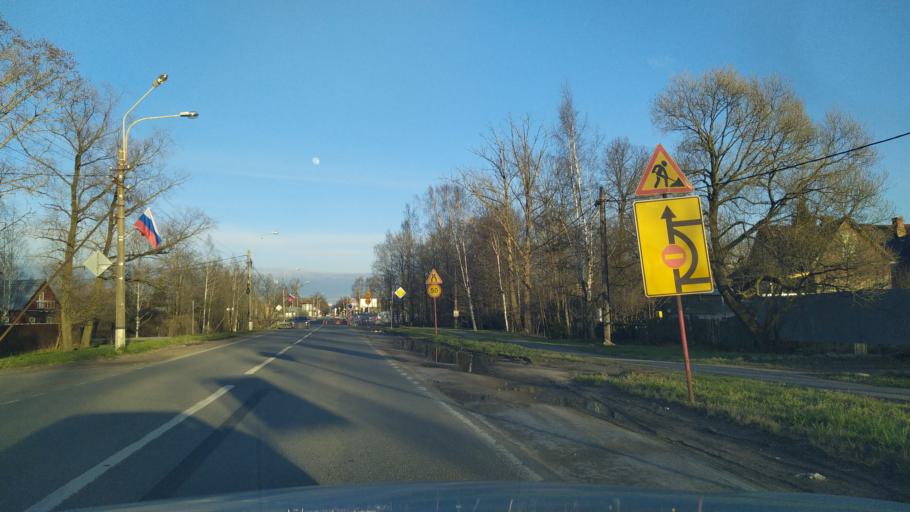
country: RU
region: St.-Petersburg
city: Aleksandrovskaya
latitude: 59.7346
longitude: 30.3374
